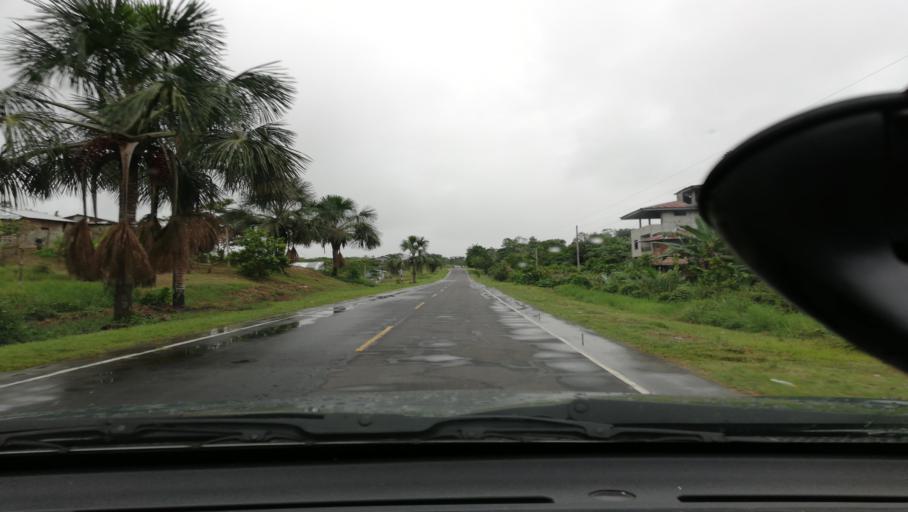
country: PE
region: Loreto
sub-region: Provincia de Maynas
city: San Juan
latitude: -4.0251
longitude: -73.4342
